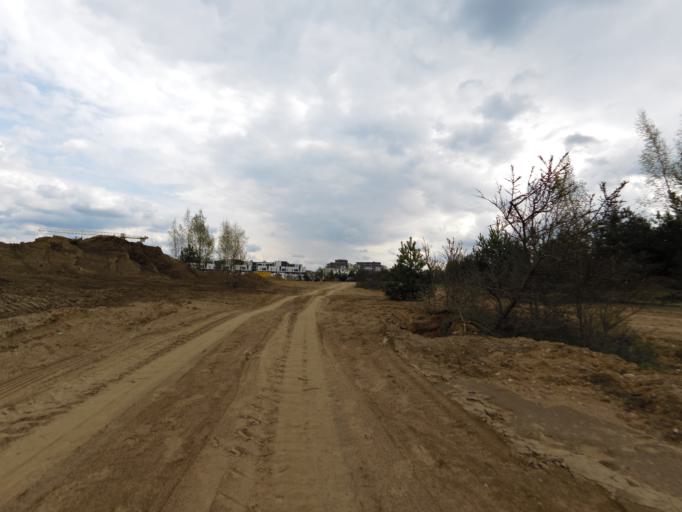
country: LT
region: Vilnius County
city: Pilaite
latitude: 54.7056
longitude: 25.1665
